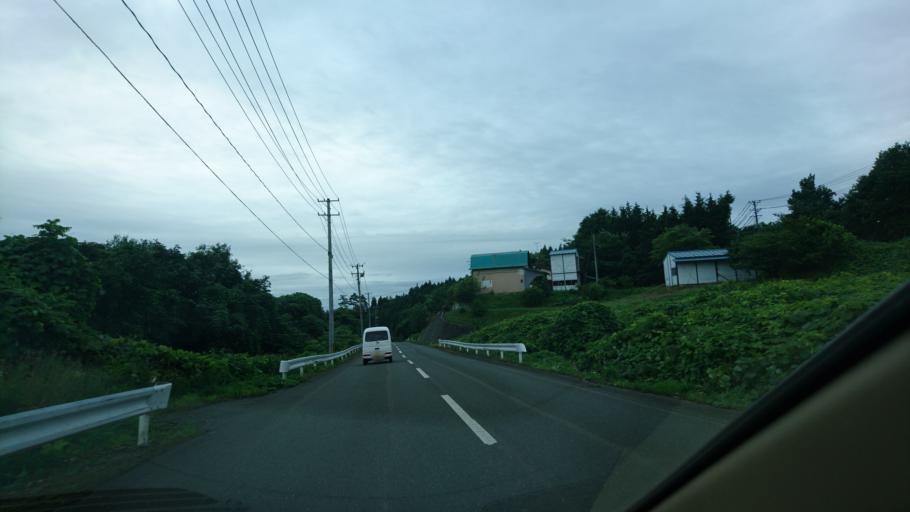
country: JP
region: Iwate
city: Mizusawa
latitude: 39.1895
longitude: 141.1999
